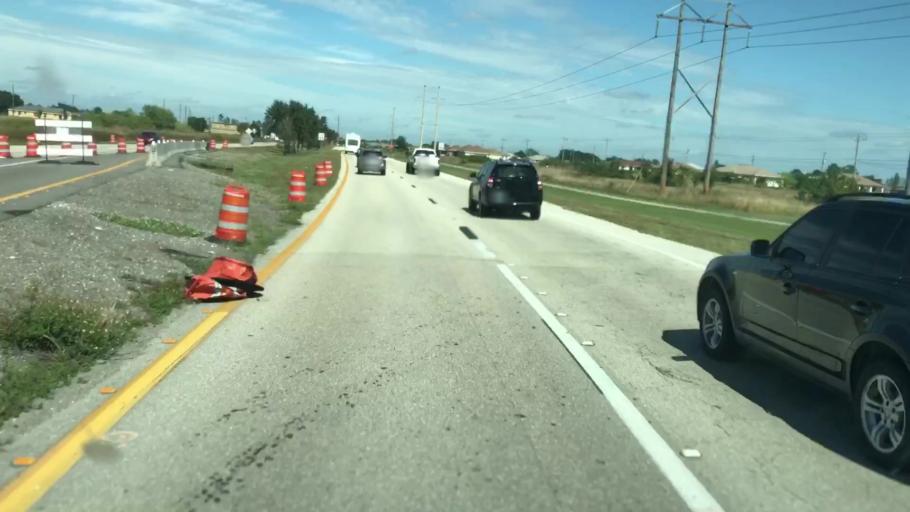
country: US
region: Florida
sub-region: Lee County
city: Gateway
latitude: 26.5852
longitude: -81.7123
